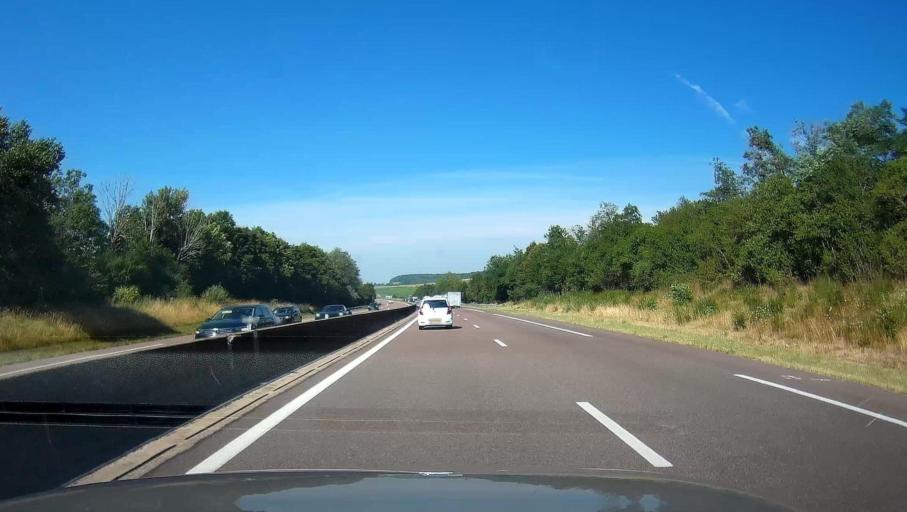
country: FR
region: Champagne-Ardenne
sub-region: Departement de la Haute-Marne
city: Nogent-le-Bas
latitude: 47.9583
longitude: 5.3910
